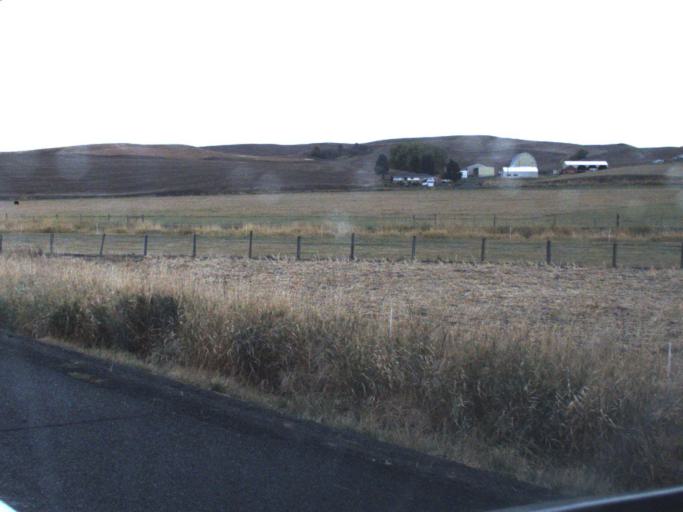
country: US
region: Washington
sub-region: Whitman County
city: Pullman
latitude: 46.5775
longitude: -117.1509
